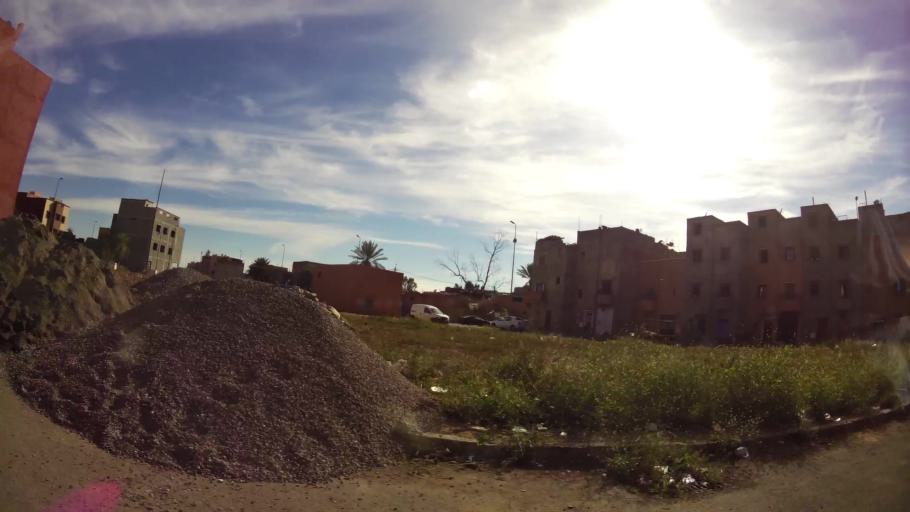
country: MA
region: Marrakech-Tensift-Al Haouz
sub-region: Marrakech
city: Marrakesh
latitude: 31.6788
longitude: -8.0577
